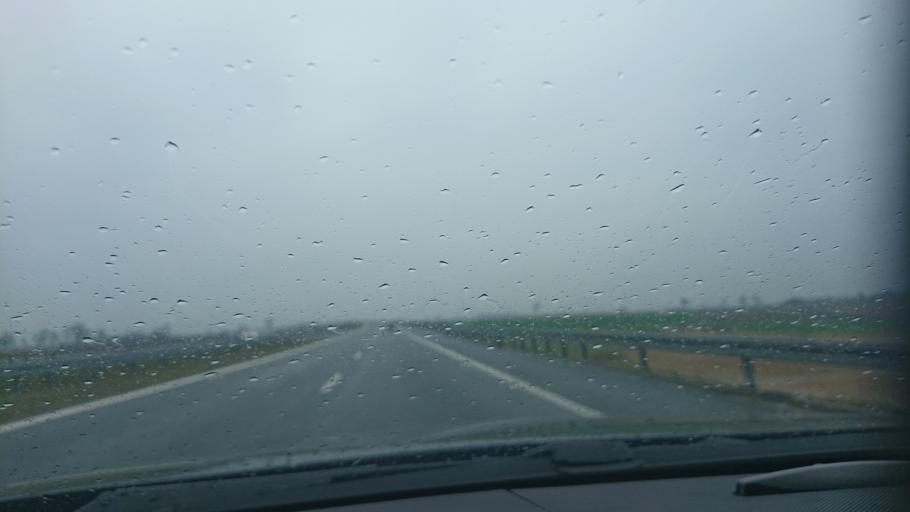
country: PL
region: Greater Poland Voivodeship
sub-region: Powiat gnieznienski
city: Gniezno
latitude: 52.5710
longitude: 17.5849
